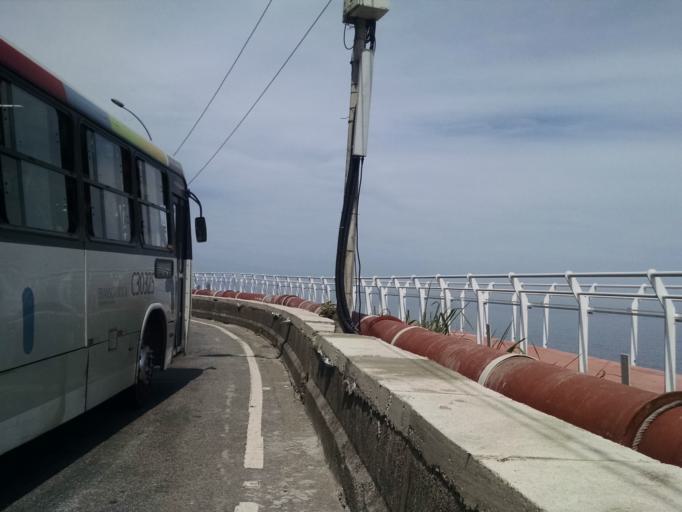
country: BR
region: Rio de Janeiro
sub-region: Rio De Janeiro
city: Rio de Janeiro
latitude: -23.0002
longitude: -43.2417
